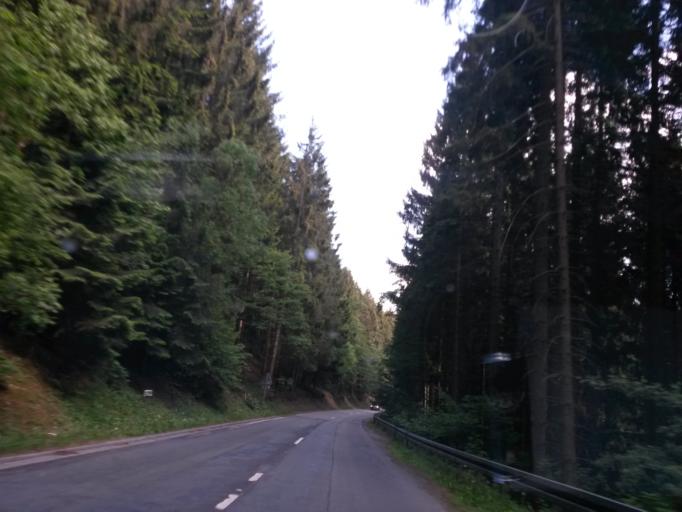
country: DE
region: North Rhine-Westphalia
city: Plettenberg
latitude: 51.2479
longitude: 7.8639
